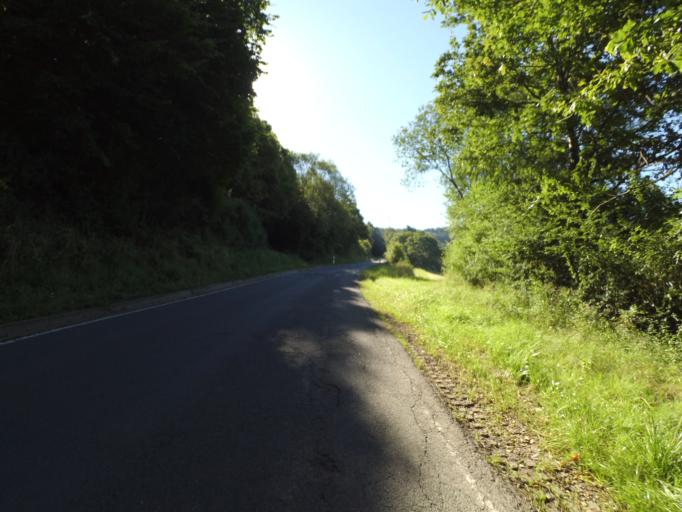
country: DE
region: Rheinland-Pfalz
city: Niederstadtfeld
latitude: 50.1736
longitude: 6.7752
